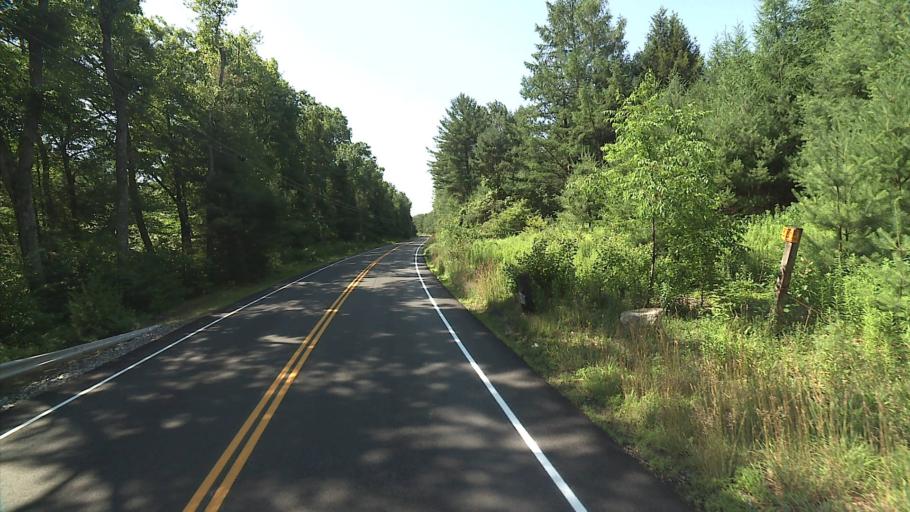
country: US
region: Connecticut
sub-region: Litchfield County
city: Terryville
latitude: 41.7289
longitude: -73.0140
